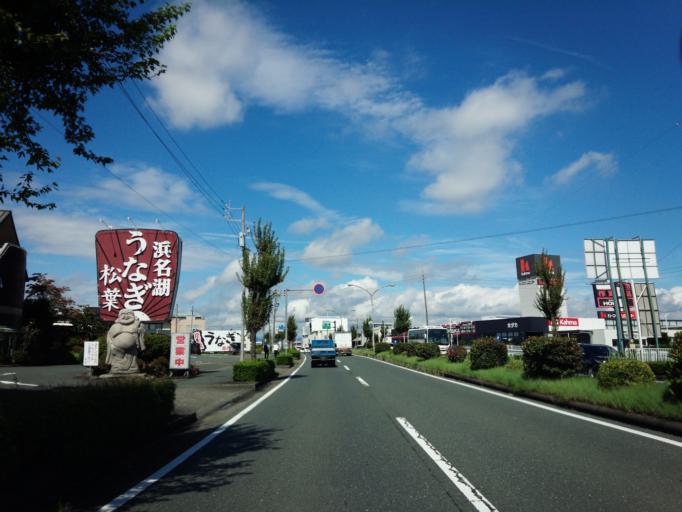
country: JP
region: Shizuoka
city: Hamakita
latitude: 34.7381
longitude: 137.7897
